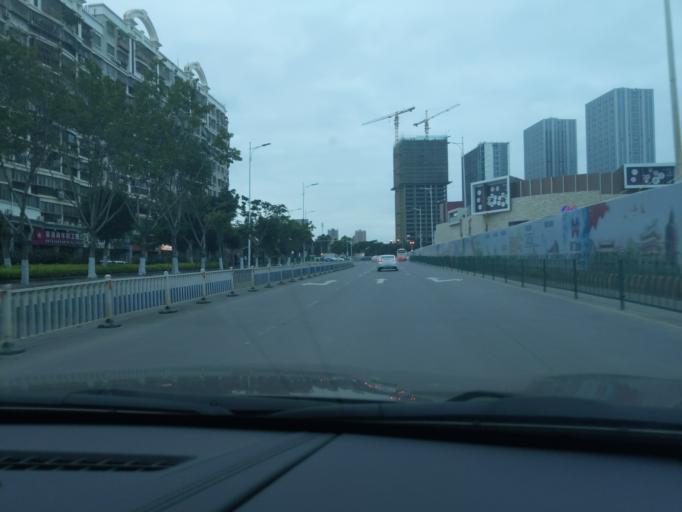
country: CN
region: Fujian
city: Liuwudian
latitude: 24.4865
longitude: 118.1710
